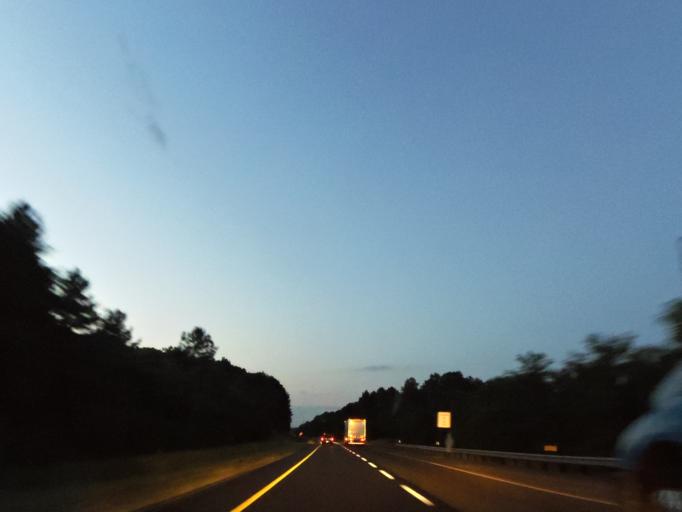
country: US
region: Tennessee
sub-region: Bradley County
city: Hopewell
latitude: 35.2760
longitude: -84.8210
